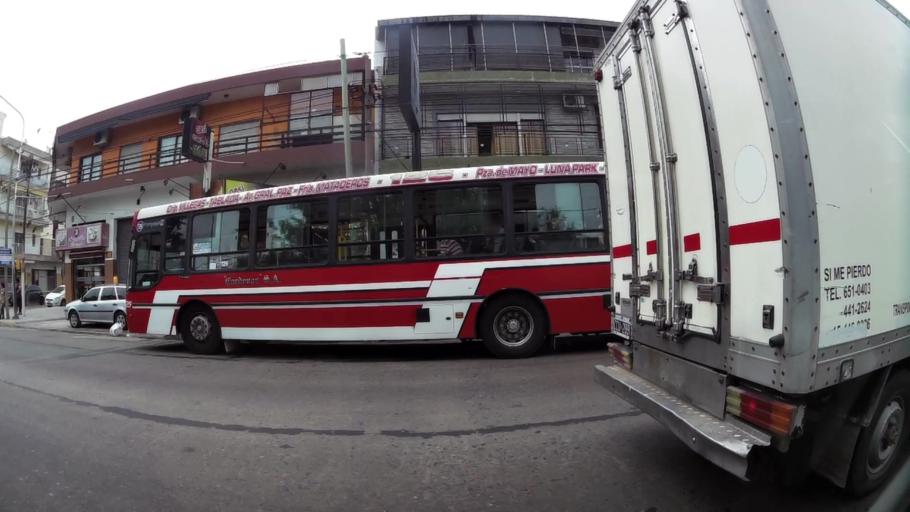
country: AR
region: Buenos Aires
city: San Justo
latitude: -34.6917
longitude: -58.5282
